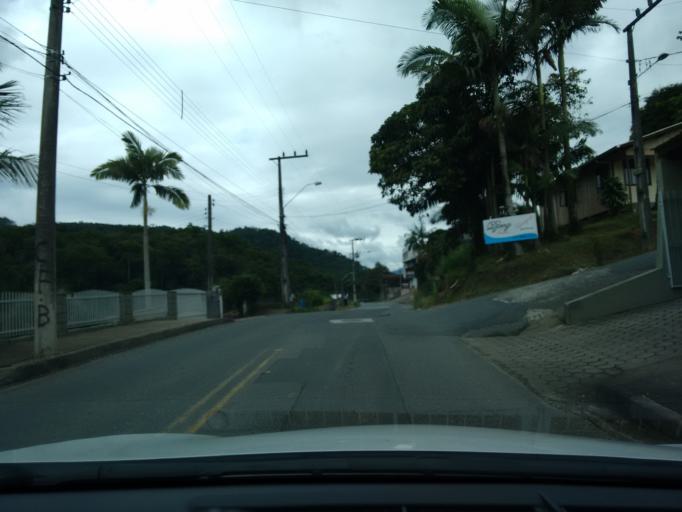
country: BR
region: Santa Catarina
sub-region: Blumenau
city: Blumenau
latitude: -26.8581
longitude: -49.1370
